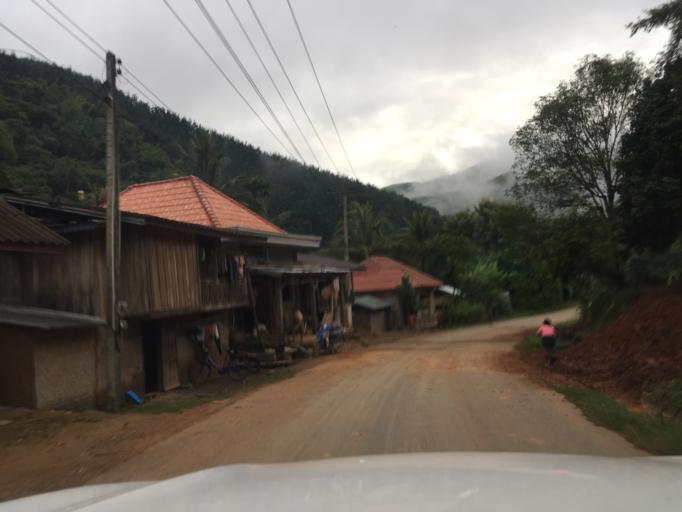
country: LA
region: Phongsali
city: Khoa
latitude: 21.0712
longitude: 102.3750
